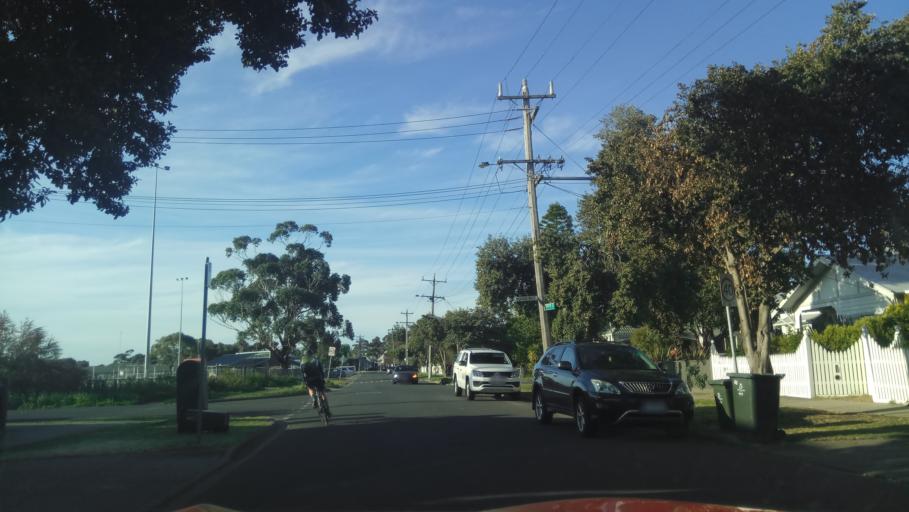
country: AU
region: Victoria
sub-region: Hobsons Bay
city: Williamstown North
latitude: -37.8607
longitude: 144.8864
